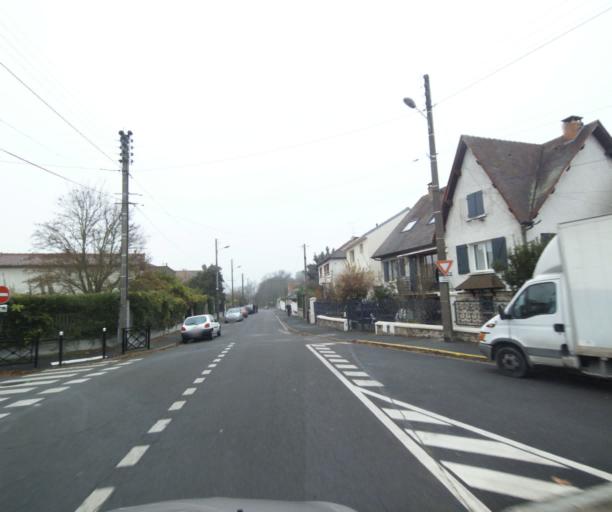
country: FR
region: Ile-de-France
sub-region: Departement de Seine-Saint-Denis
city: Gagny
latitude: 48.8736
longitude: 2.5464
